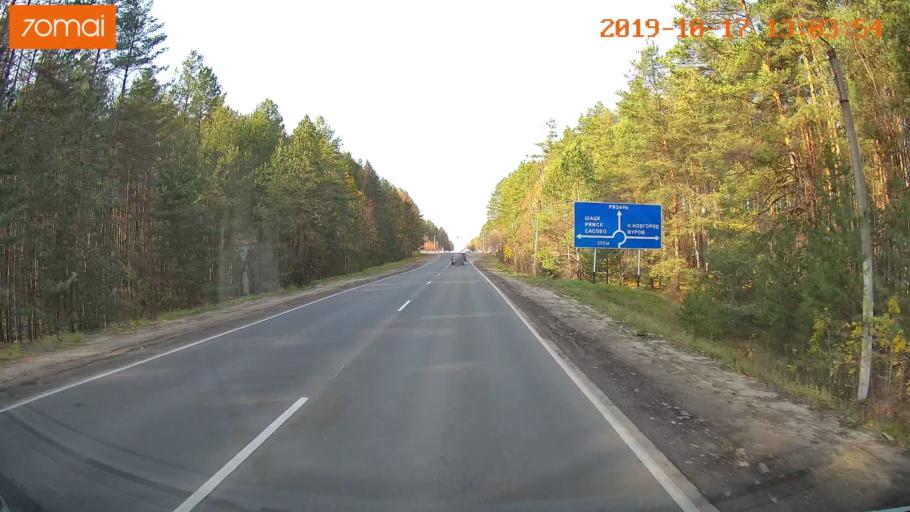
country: RU
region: Rjazan
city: Kasimov
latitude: 54.9584
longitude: 41.3488
